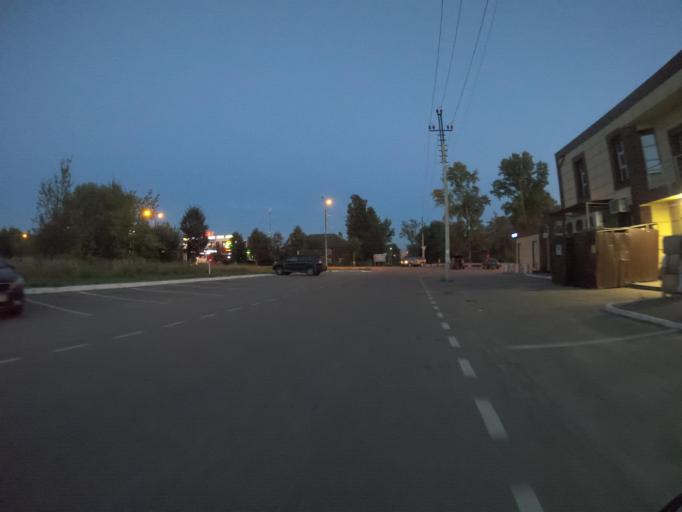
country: RU
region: Moskovskaya
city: Mikhnevo
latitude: 55.1203
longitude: 37.9525
